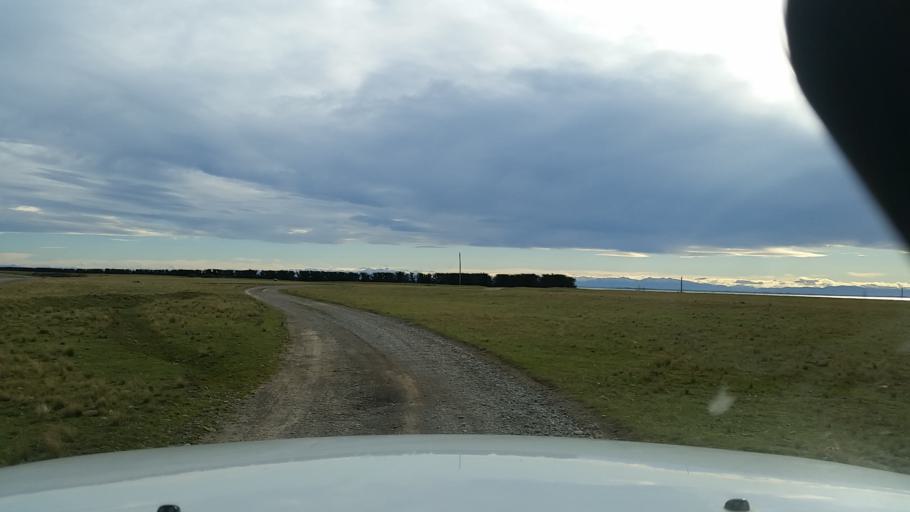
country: NZ
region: Canterbury
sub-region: Selwyn District
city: Lincoln
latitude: -43.8150
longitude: 172.6387
